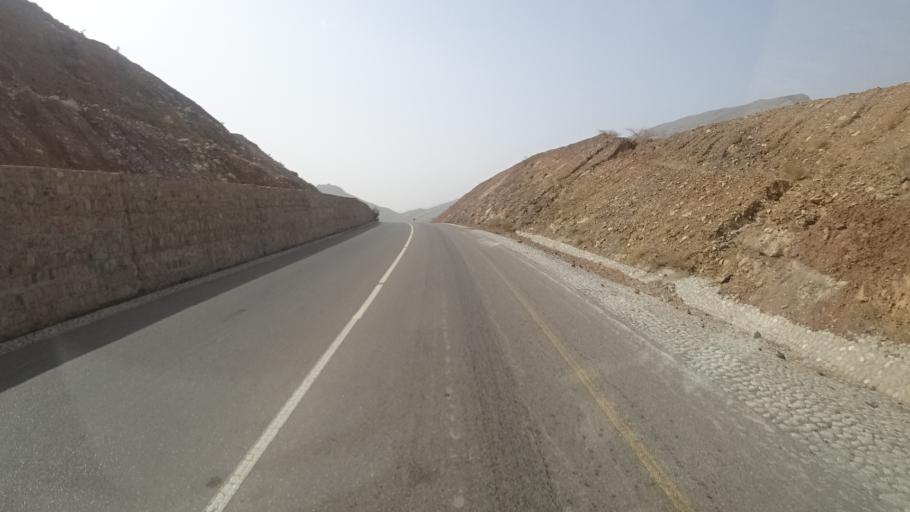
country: OM
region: Muhafazat ad Dakhiliyah
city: Nizwa
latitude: 23.0029
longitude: 57.5785
